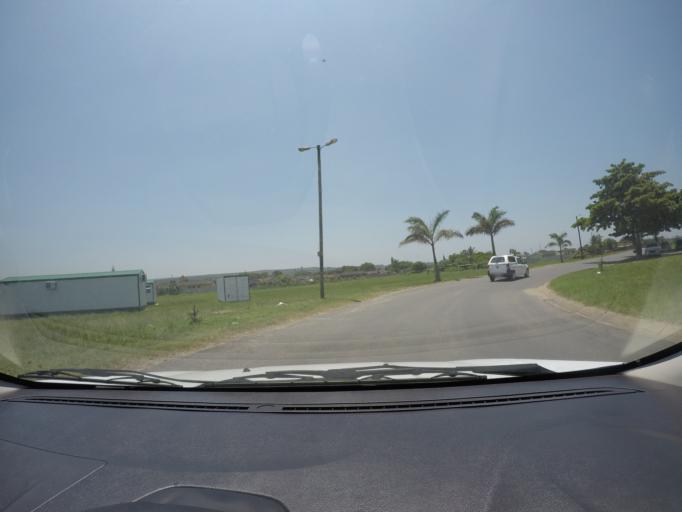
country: ZA
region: KwaZulu-Natal
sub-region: uThungulu District Municipality
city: eSikhawini
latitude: -28.8898
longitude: 31.8922
